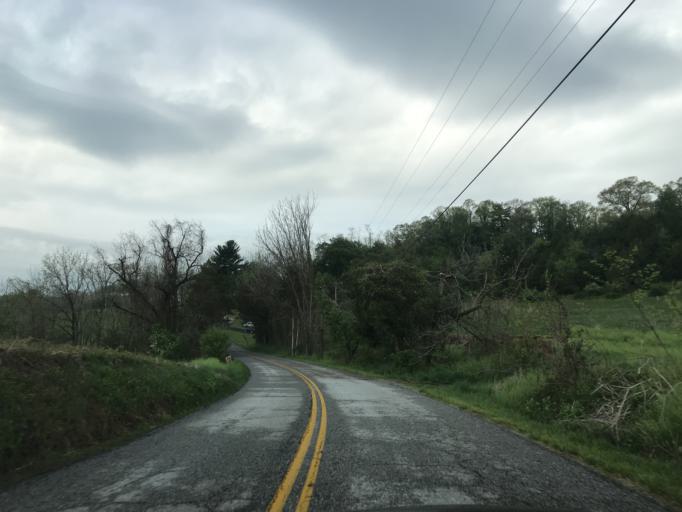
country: US
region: Maryland
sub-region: Harford County
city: Jarrettsville
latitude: 39.6714
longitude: -76.4541
